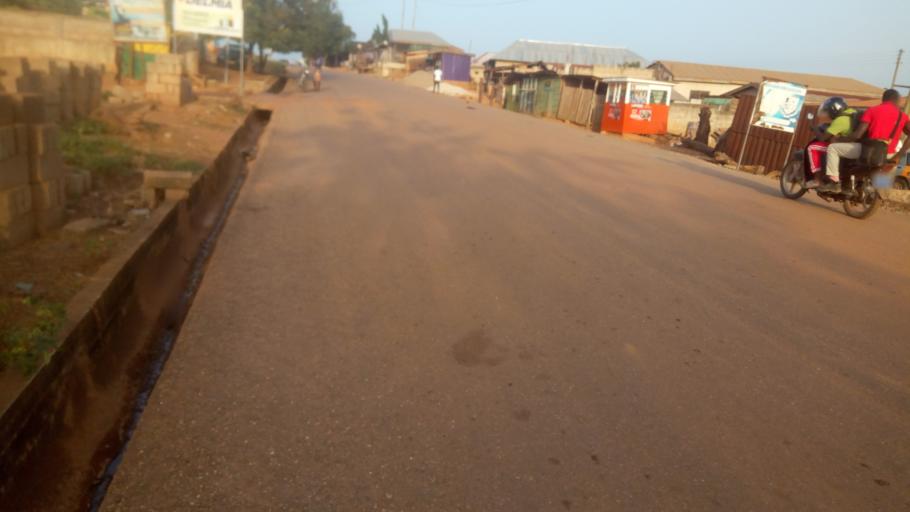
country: GH
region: Ashanti
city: Obuasi
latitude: 6.2127
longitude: -1.6958
